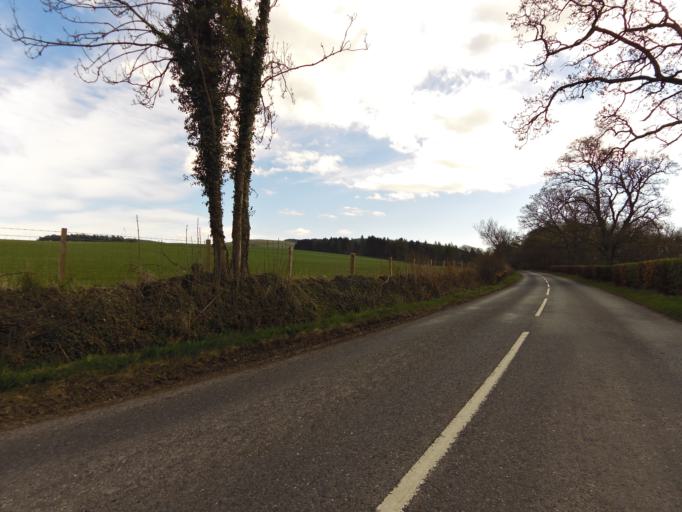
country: GB
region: Scotland
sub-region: Fife
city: Newburgh
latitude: 56.3307
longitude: -3.2303
